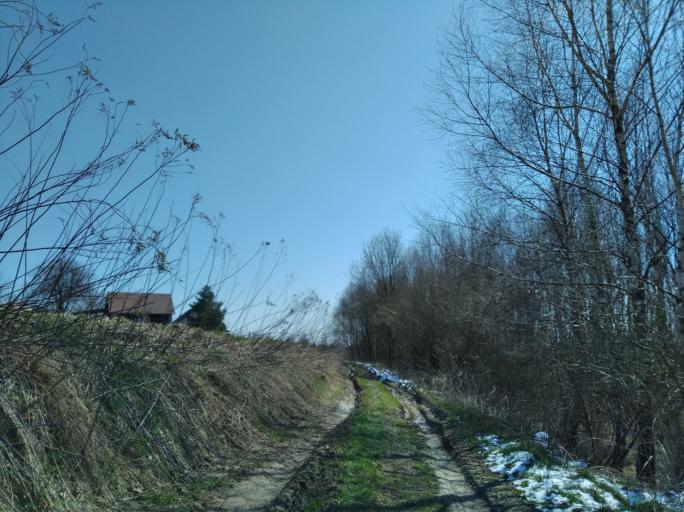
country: PL
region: Subcarpathian Voivodeship
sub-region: Powiat strzyzowski
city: Strzyzow
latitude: 49.8510
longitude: 21.8236
